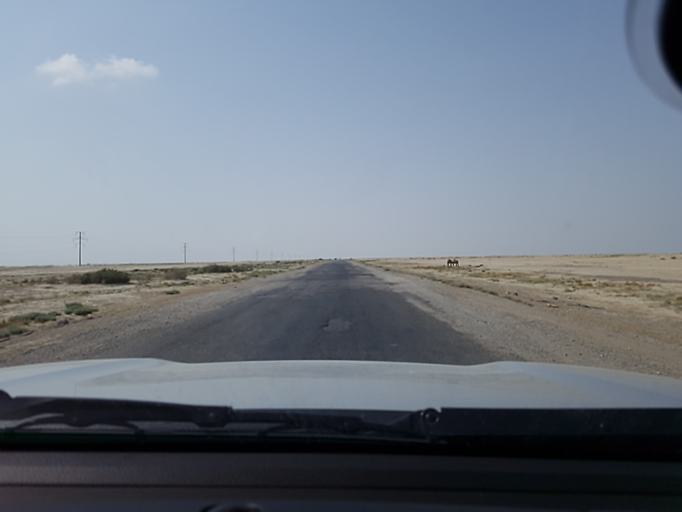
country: TM
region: Balkan
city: Gumdag
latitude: 38.8945
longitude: 54.5927
